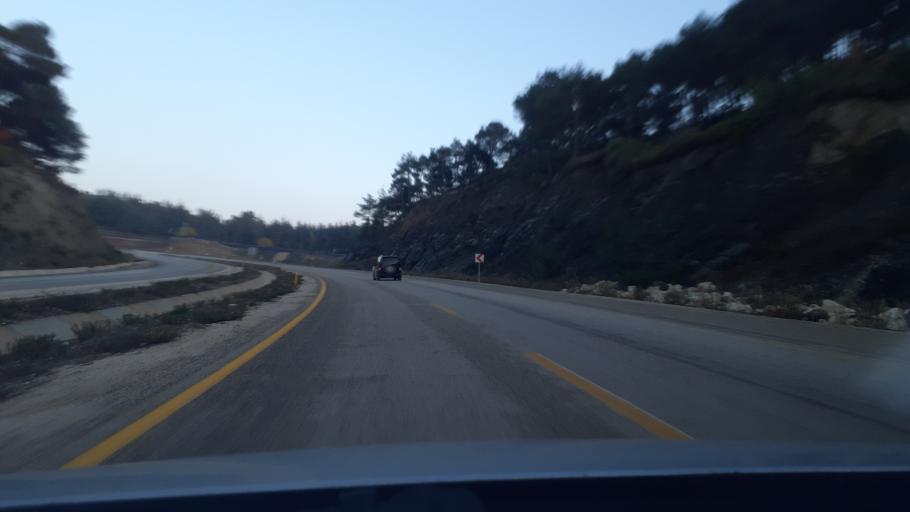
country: TR
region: Hatay
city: Yayladagi
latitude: 35.8906
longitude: 36.0886
